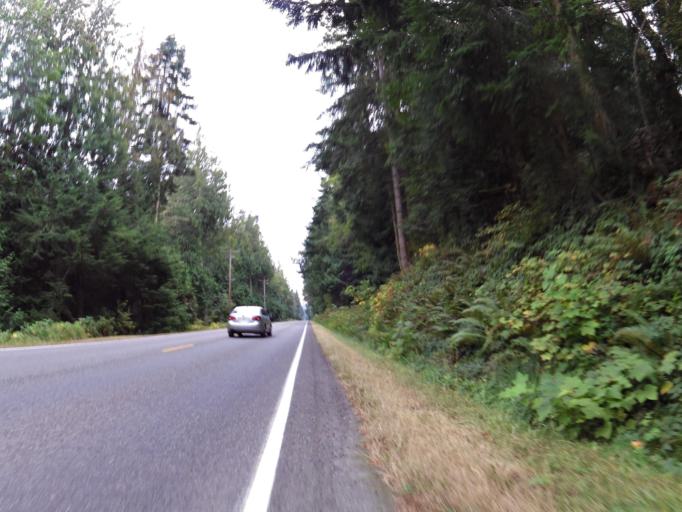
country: US
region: Washington
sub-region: Jefferson County
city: Port Hadlock-Irondale
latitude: 48.0010
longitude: -122.7242
